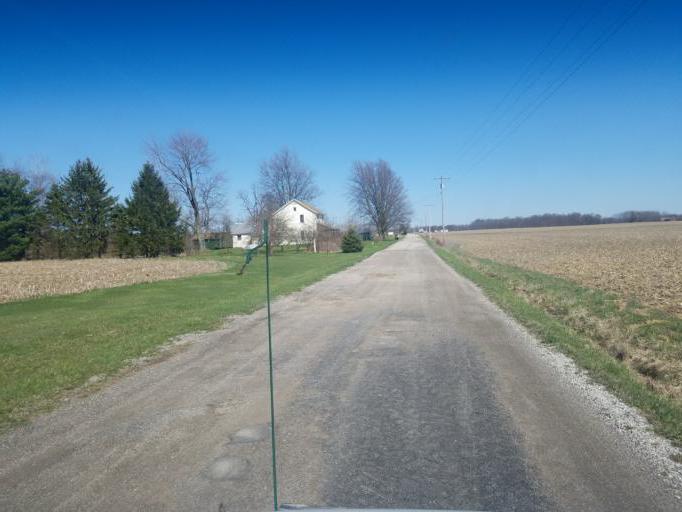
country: US
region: Ohio
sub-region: Morrow County
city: Mount Gilead
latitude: 40.5866
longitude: -82.8978
